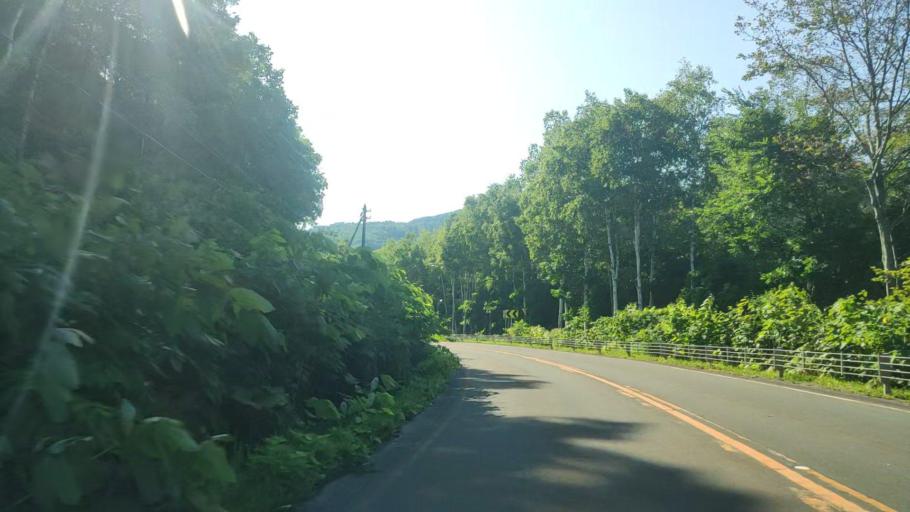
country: JP
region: Hokkaido
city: Nayoro
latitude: 44.7383
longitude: 142.1870
